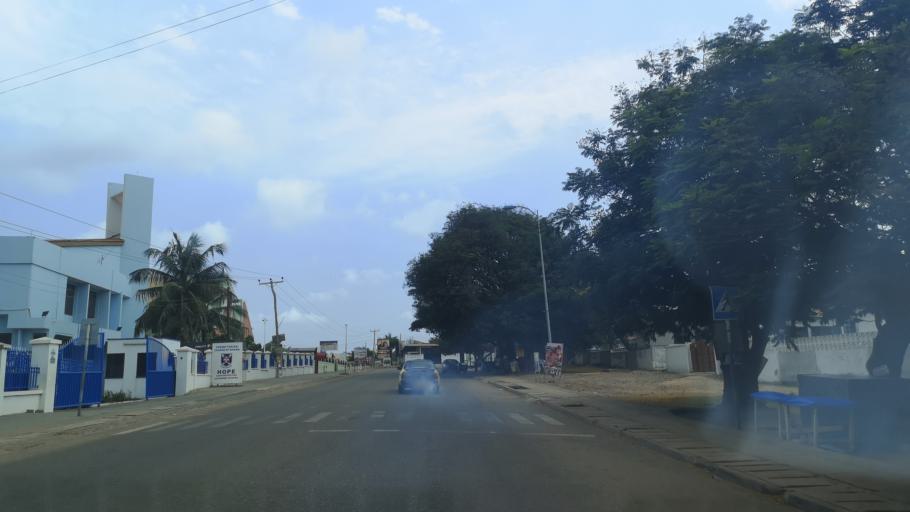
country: GH
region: Greater Accra
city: Nungua
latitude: 5.6222
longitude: -0.0612
